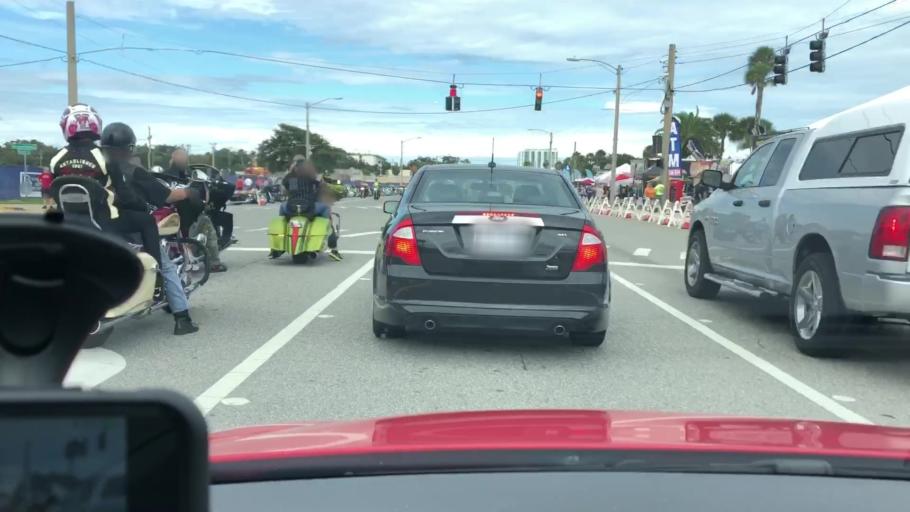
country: US
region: Florida
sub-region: Volusia County
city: Daytona Beach
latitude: 29.2167
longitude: -81.0216
